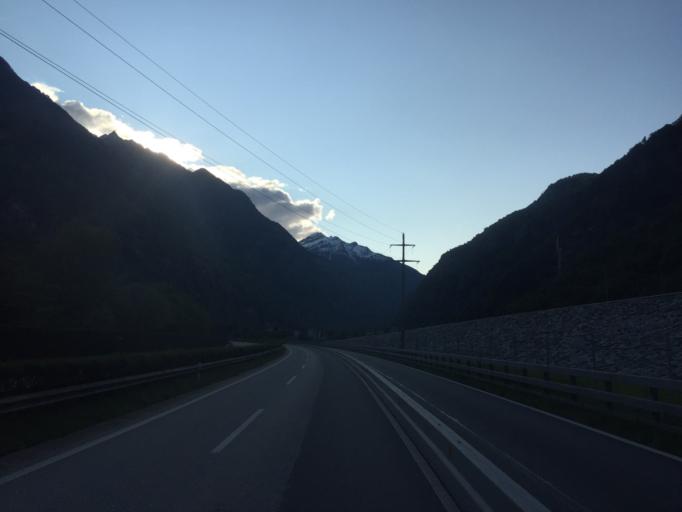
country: CH
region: Ticino
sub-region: Leventina District
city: Bodio
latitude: 46.3726
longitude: 8.9248
